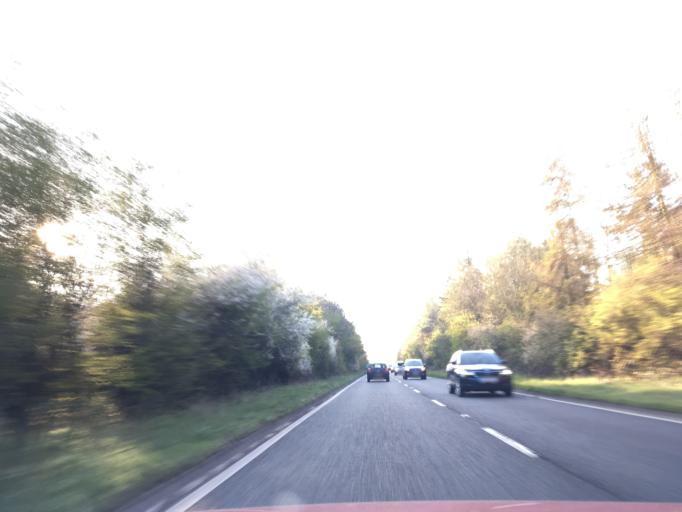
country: GB
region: England
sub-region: Gloucestershire
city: Northleach
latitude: 51.8353
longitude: -1.8284
